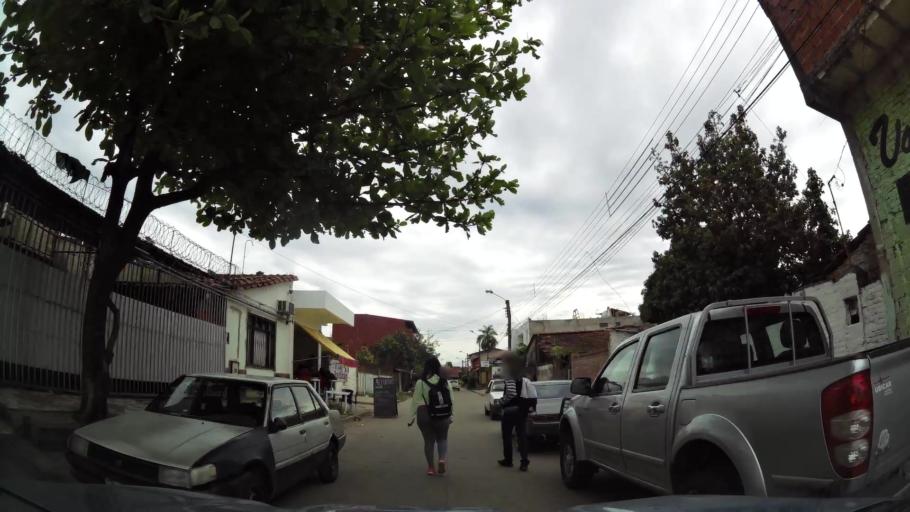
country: BO
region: Santa Cruz
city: Santa Cruz de la Sierra
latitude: -17.7705
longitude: -63.2023
